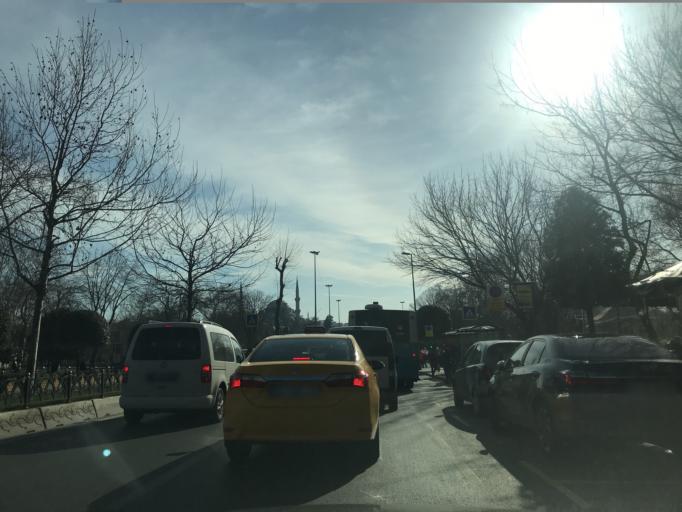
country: TR
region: Istanbul
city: Istanbul
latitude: 41.0158
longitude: 28.9524
